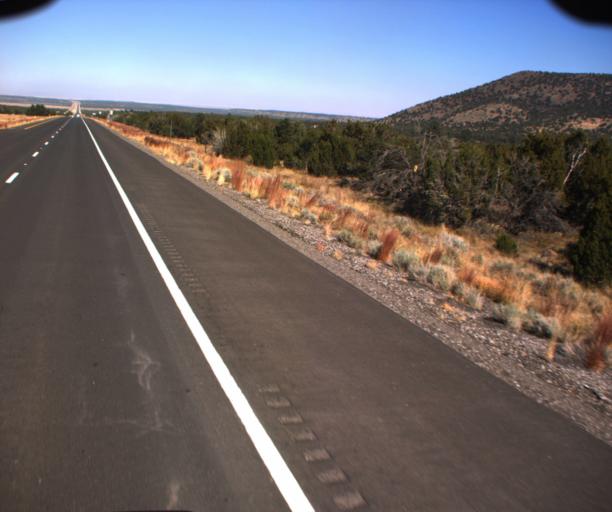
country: US
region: Arizona
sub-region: Coconino County
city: Flagstaff
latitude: 35.4045
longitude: -111.5748
